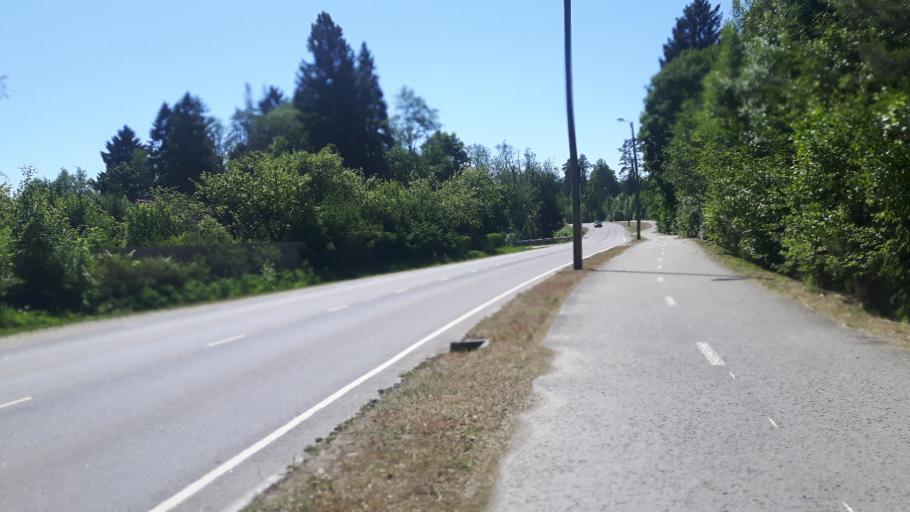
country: EE
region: Harju
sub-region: Saku vald
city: Saku
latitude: 59.2290
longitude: 24.6785
